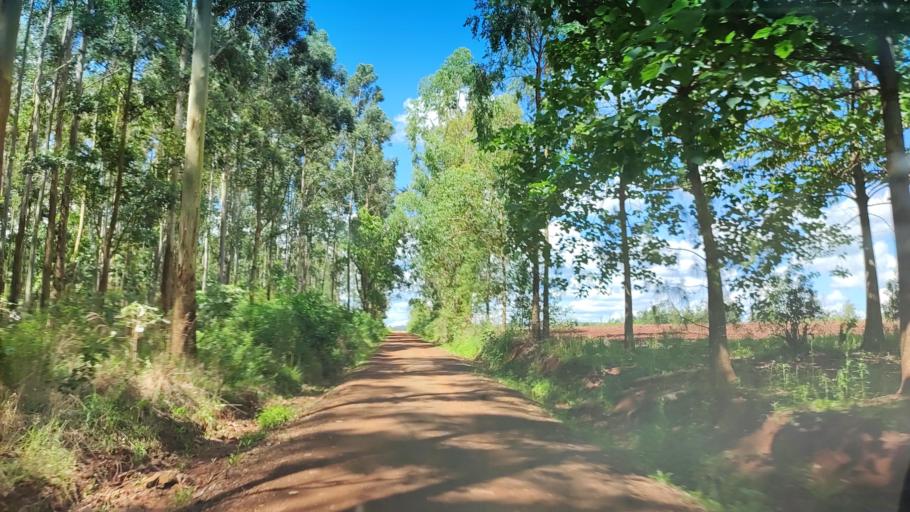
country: AR
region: Misiones
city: Ruiz de Montoya
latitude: -26.9529
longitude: -55.0219
